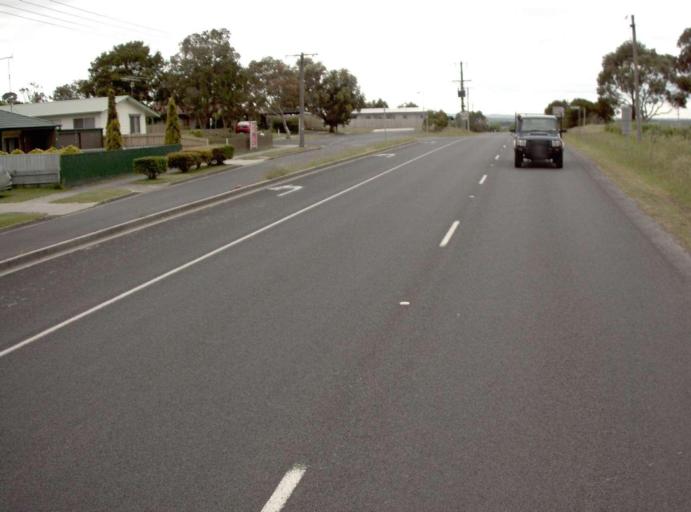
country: AU
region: Victoria
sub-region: Bass Coast
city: North Wonthaggi
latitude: -38.6003
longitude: 145.6028
